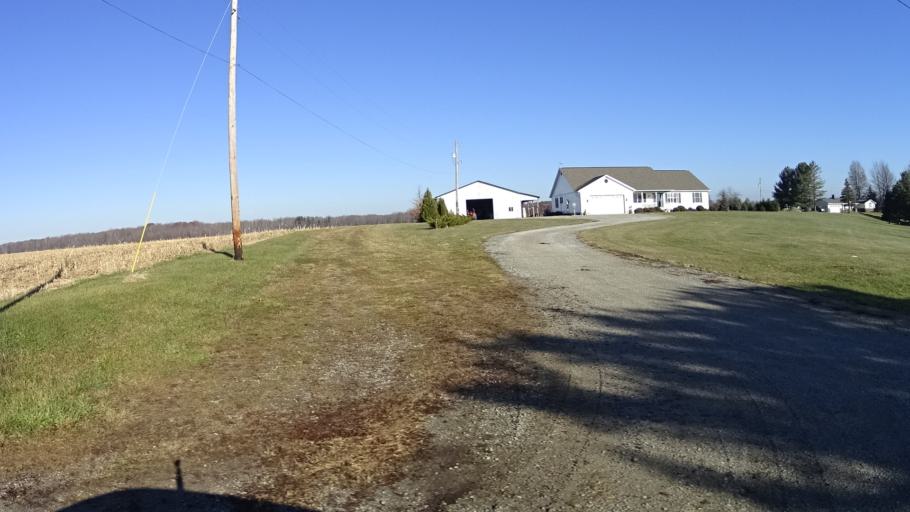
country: US
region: Ohio
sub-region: Lorain County
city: Wellington
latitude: 41.1369
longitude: -82.1436
